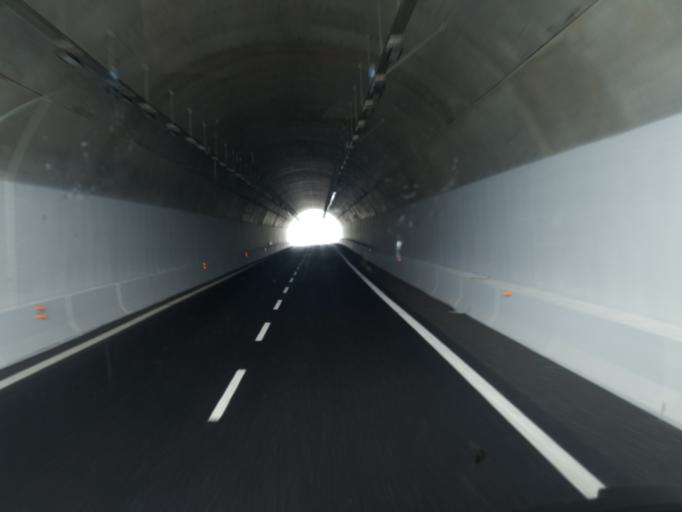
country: IT
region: Latium
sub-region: Provincia di Viterbo
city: Monte Romano
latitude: 42.2970
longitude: 11.9549
